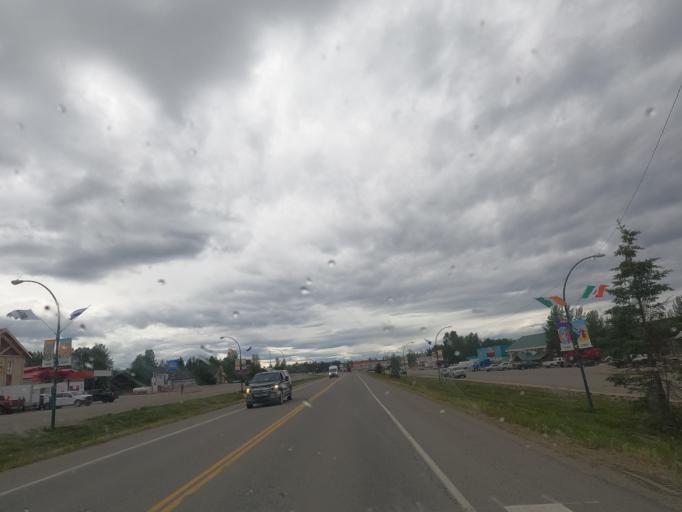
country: CA
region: Yukon
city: Watson Lake
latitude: 60.0620
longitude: -128.7033
